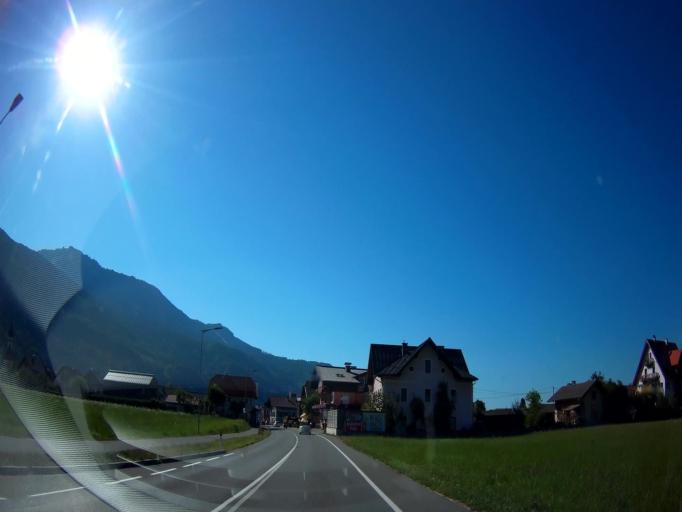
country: AT
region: Salzburg
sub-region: Politischer Bezirk Hallein
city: Kuchl
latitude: 47.6256
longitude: 13.1486
